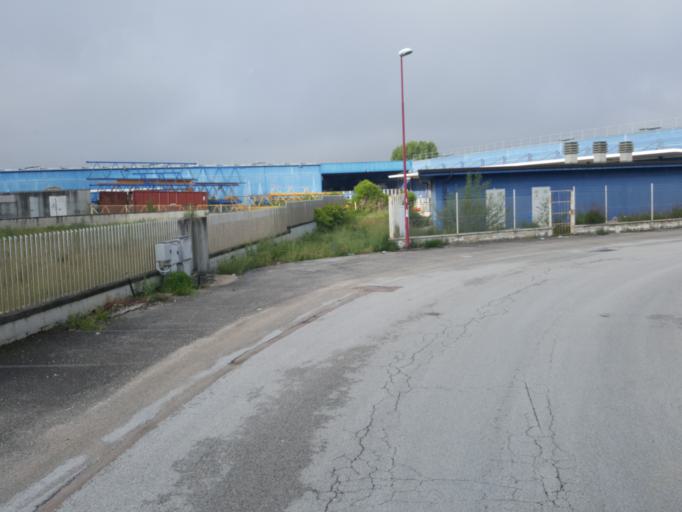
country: IT
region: Umbria
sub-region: Provincia di Perugia
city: Bastia umbra
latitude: 43.0512
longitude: 12.5515
